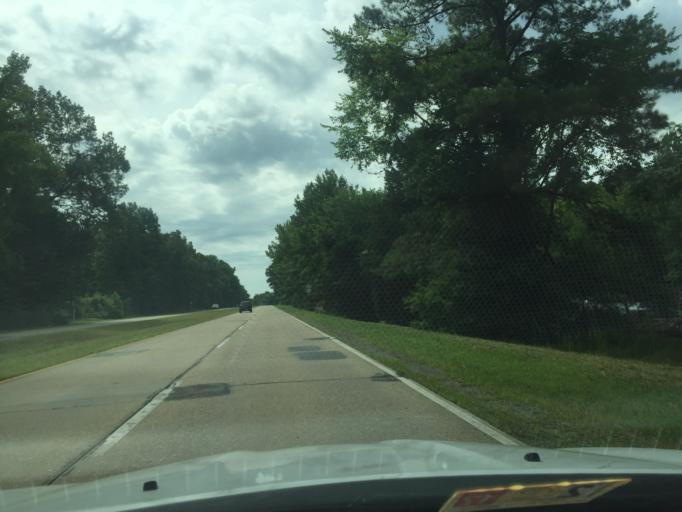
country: US
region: Virginia
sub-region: Charles City County
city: Charles City
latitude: 37.4648
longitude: -77.1062
